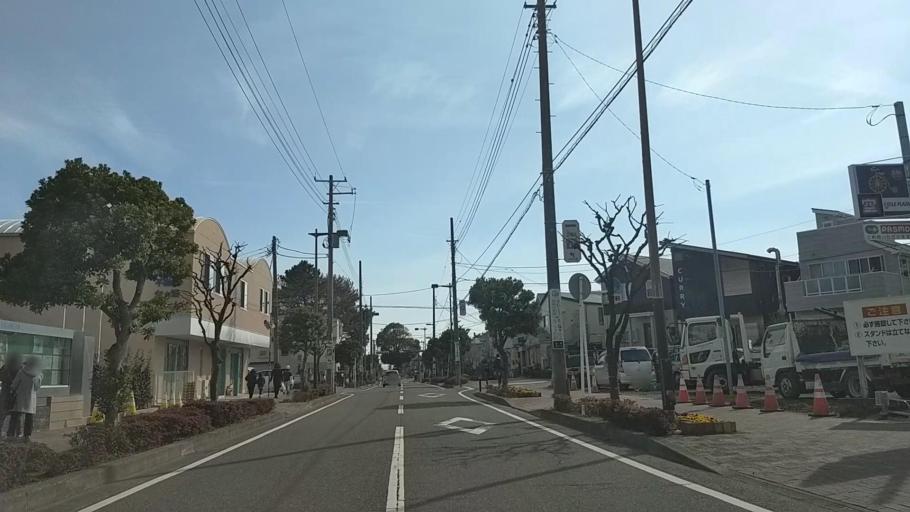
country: JP
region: Kanagawa
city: Fujisawa
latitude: 35.3352
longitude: 139.4471
